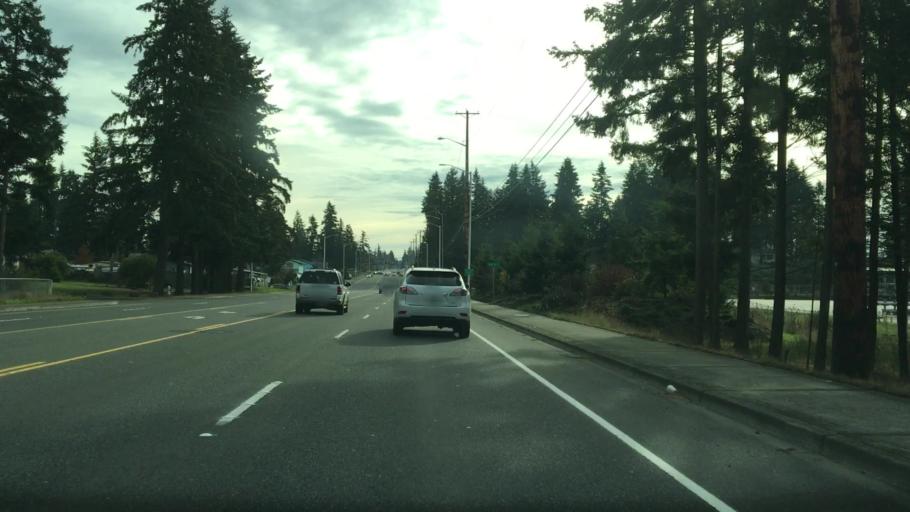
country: US
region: Washington
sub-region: Pierce County
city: South Hill
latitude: 47.1446
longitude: -122.3042
